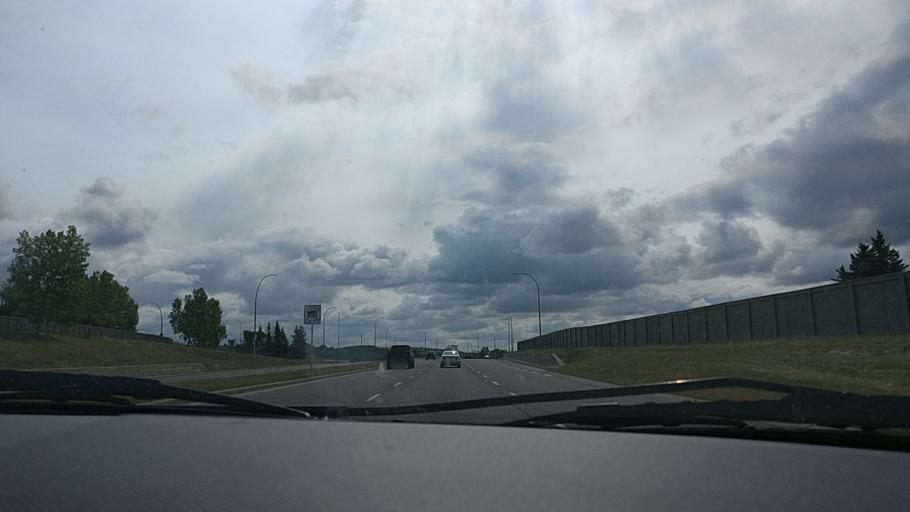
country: CA
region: Alberta
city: Calgary
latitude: 51.1106
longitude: -114.1440
